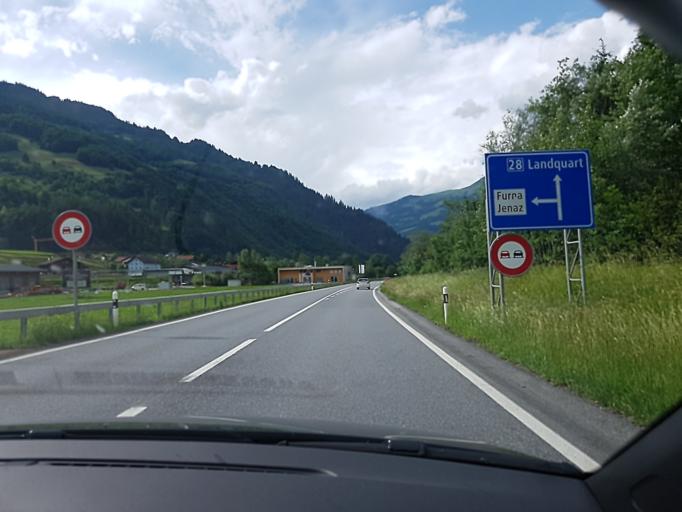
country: CH
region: Grisons
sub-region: Praettigau/Davos District
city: Jenaz
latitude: 46.9359
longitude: 9.7122
